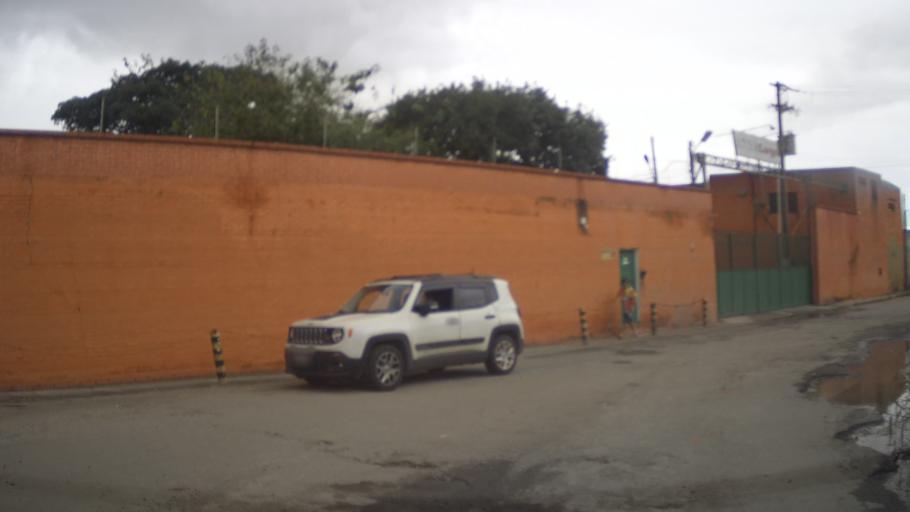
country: BR
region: Sao Paulo
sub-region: Guarulhos
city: Guarulhos
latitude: -23.4658
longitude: -46.4977
